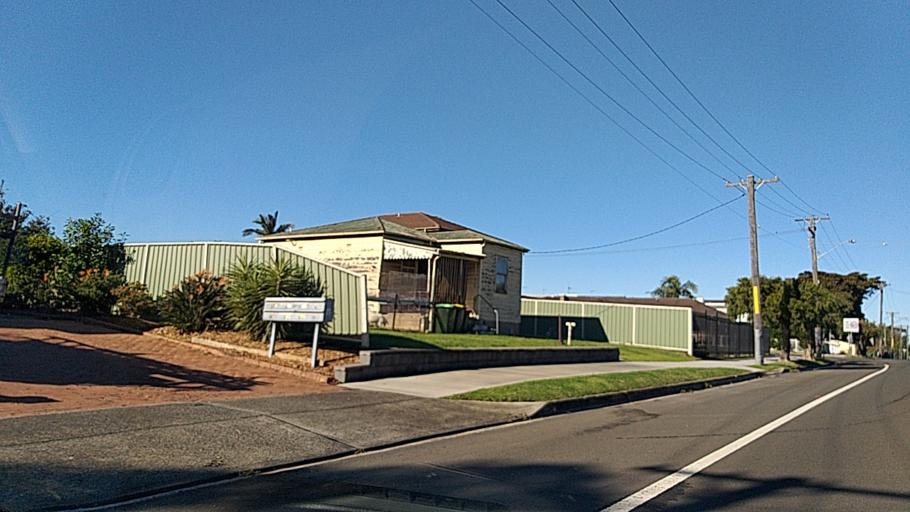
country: AU
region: New South Wales
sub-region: Wollongong
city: Berkeley
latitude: -34.4812
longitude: 150.8550
